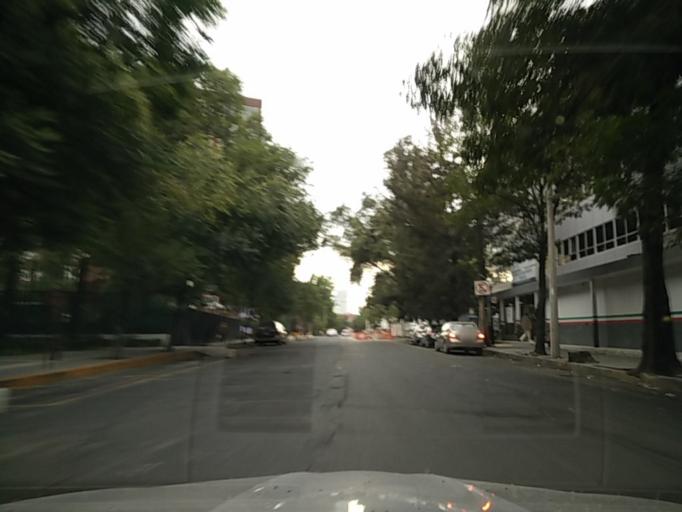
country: MX
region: Mexico City
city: Mexico City
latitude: 19.4216
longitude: -99.1489
